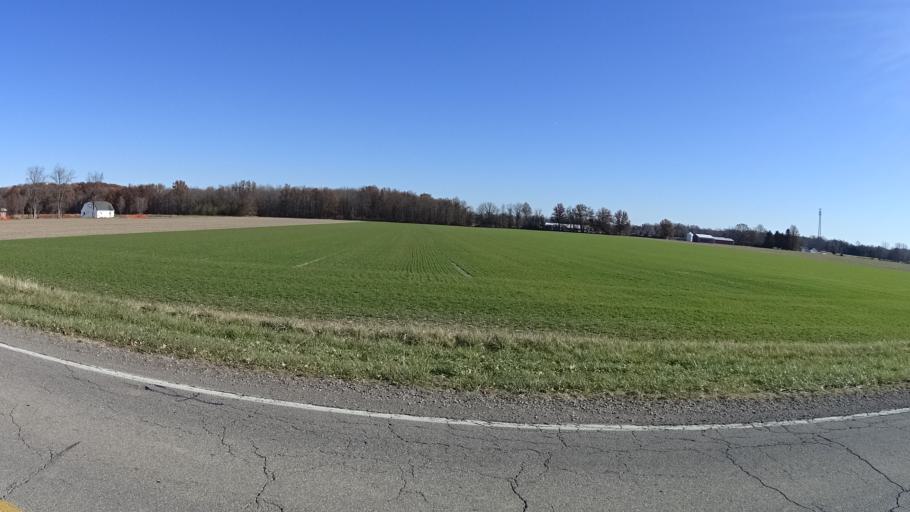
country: US
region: Ohio
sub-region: Lorain County
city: Elyria
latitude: 41.3166
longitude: -82.1519
